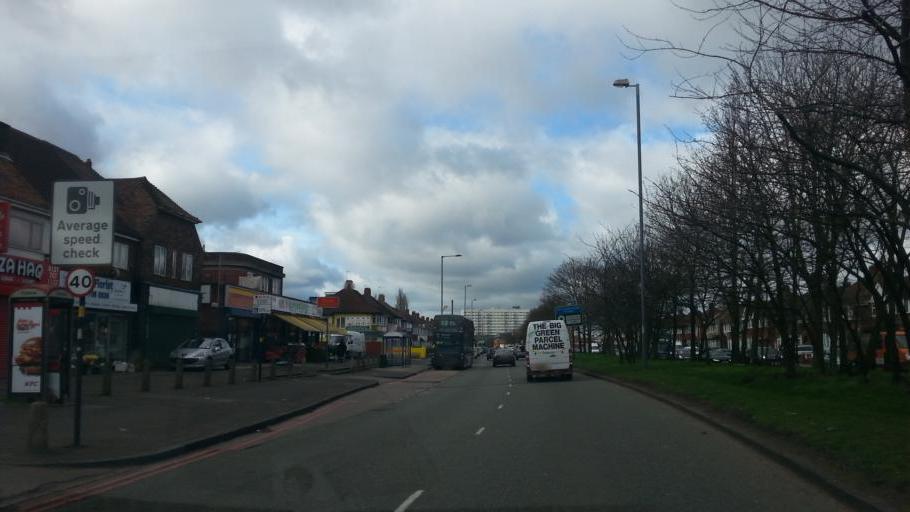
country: GB
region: England
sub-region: City and Borough of Birmingham
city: Acocks Green
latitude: 52.4610
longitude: -1.8045
